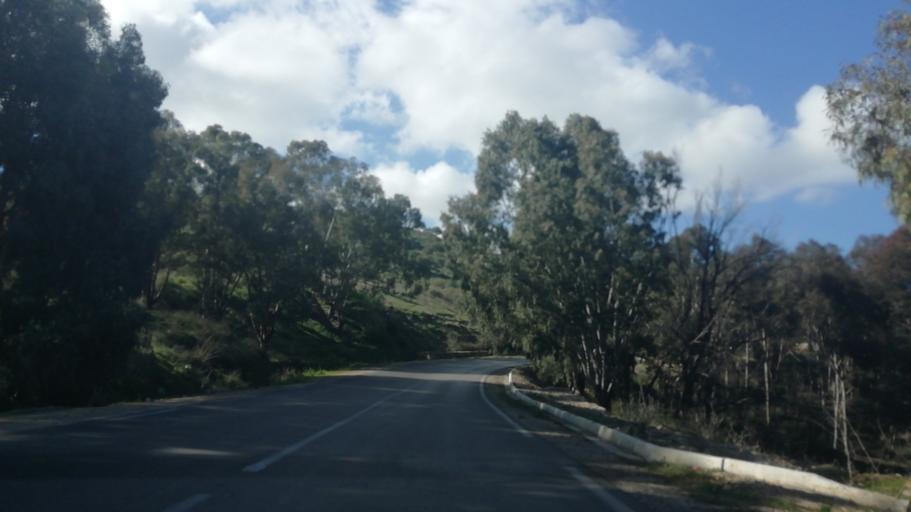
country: DZ
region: Relizane
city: Relizane
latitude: 36.0851
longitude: 0.4754
